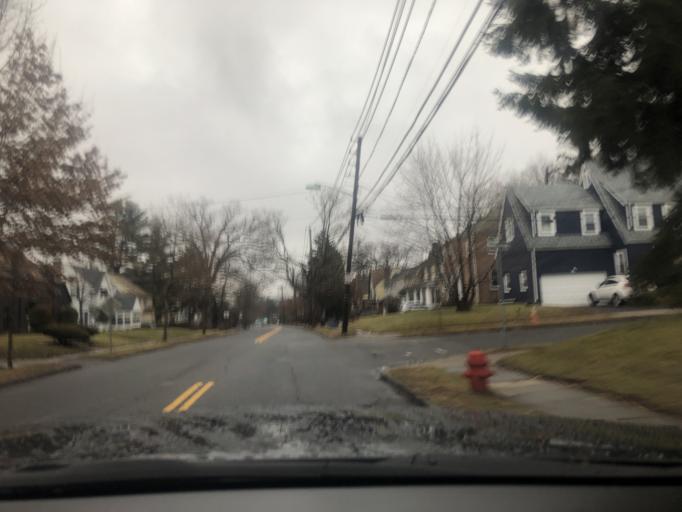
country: US
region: New Jersey
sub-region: Essex County
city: Orange
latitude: 40.7561
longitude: -74.2393
